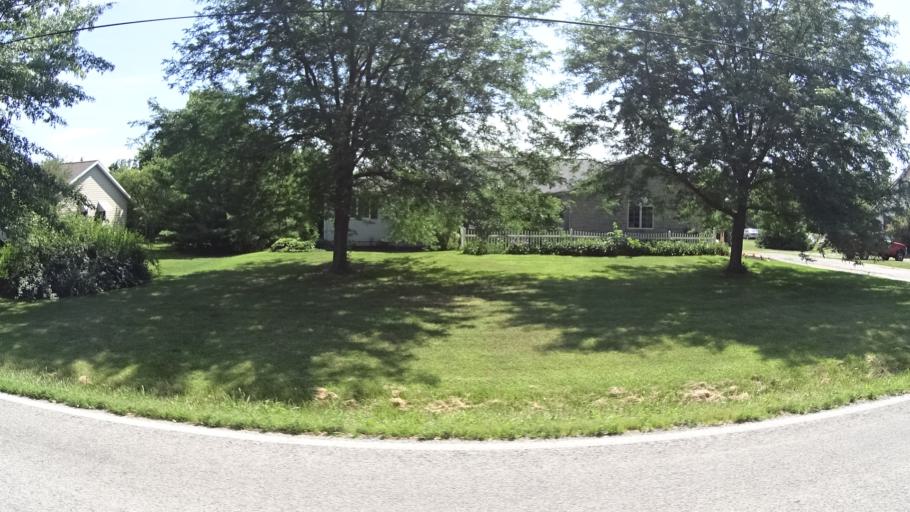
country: US
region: Ohio
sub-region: Erie County
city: Sandusky
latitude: 41.4285
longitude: -82.7722
